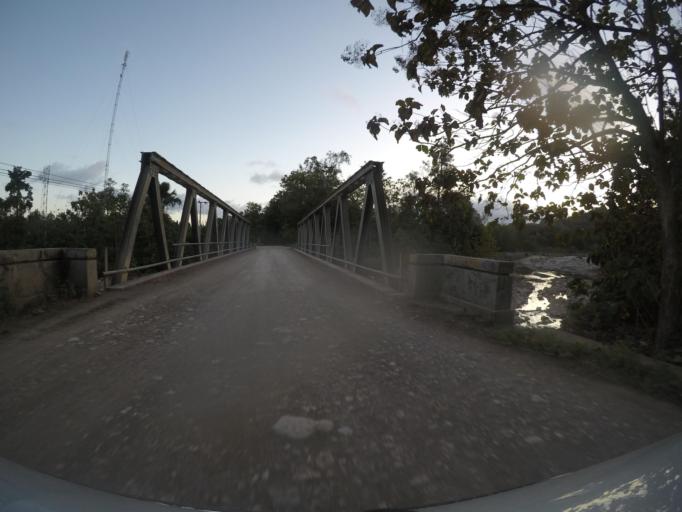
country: TL
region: Viqueque
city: Viqueque
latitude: -8.7676
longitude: 126.6442
